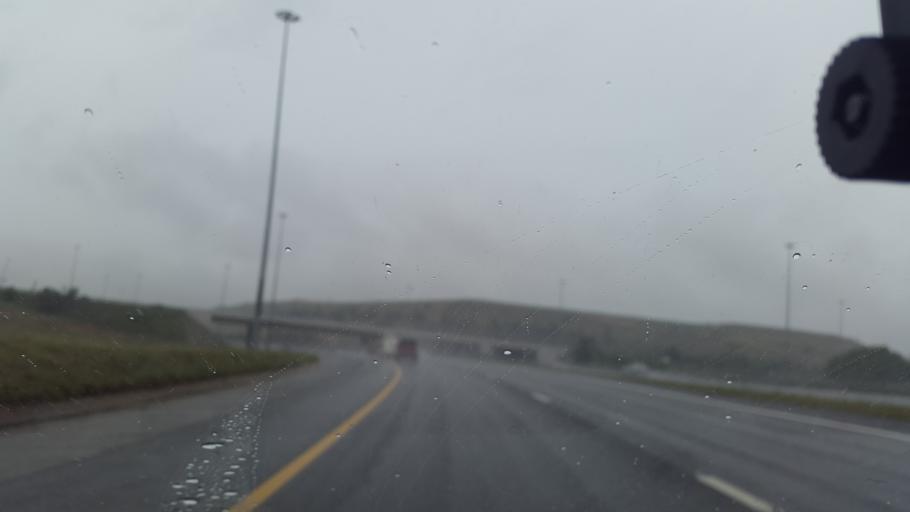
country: ZA
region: Gauteng
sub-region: City of Johannesburg Metropolitan Municipality
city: Johannesburg
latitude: -26.2522
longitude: 27.9636
